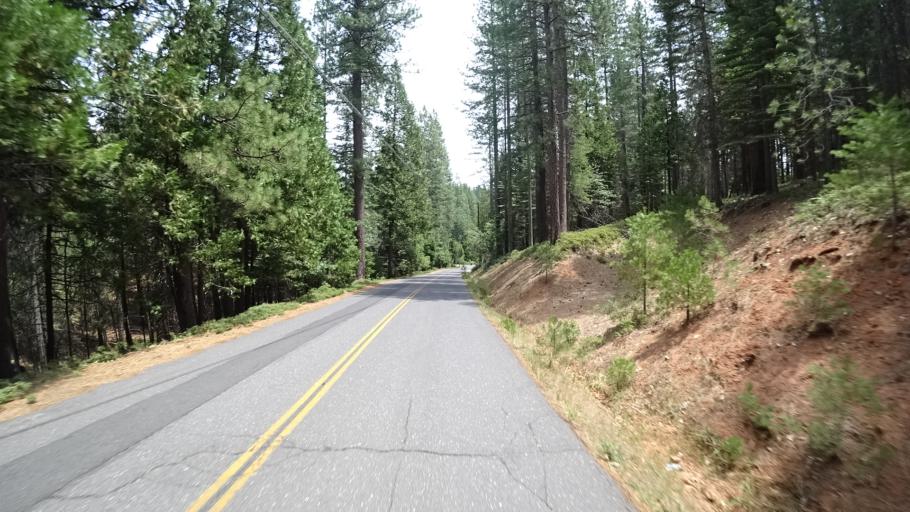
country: US
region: California
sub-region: Calaveras County
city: Arnold
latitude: 38.2385
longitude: -120.3481
